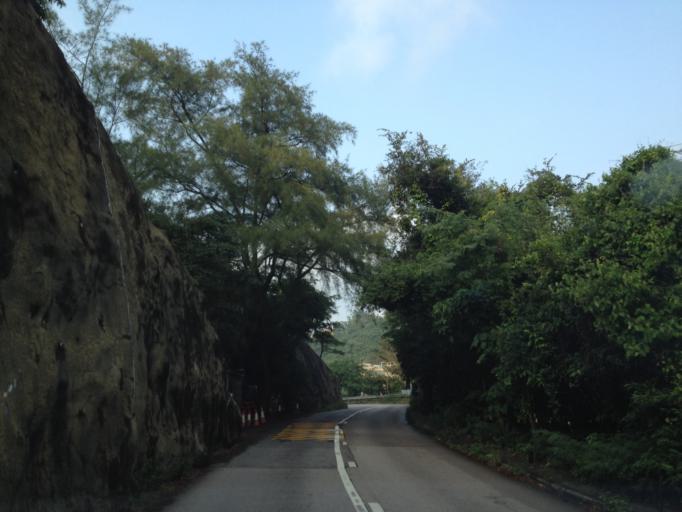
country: HK
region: Wanchai
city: Wan Chai
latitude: 22.2315
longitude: 114.2219
